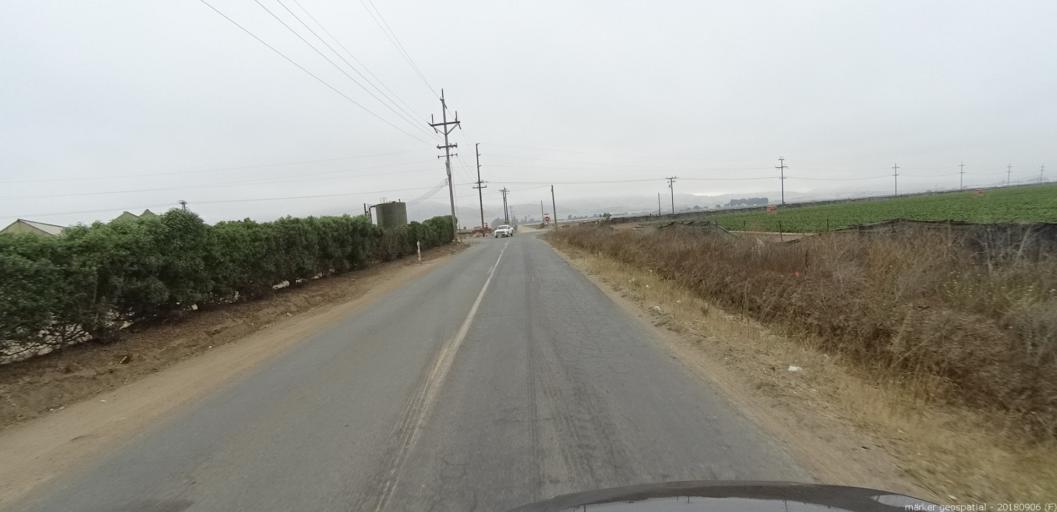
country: US
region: California
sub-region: Monterey County
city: Chualar
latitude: 36.6293
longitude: -121.5408
